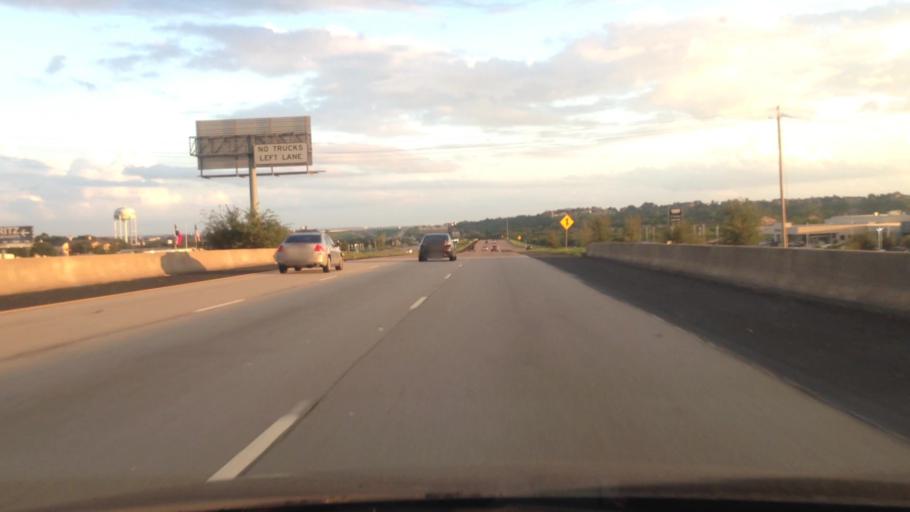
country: US
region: Texas
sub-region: Tarrant County
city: White Settlement
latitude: 32.7237
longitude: -97.4800
